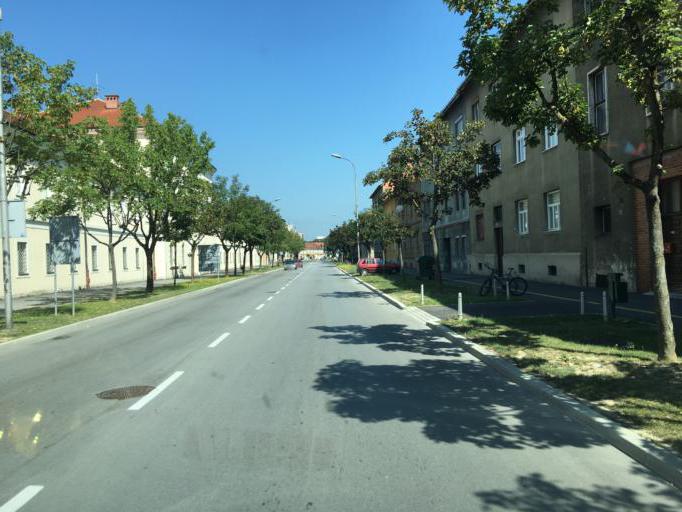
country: HR
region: Karlovacka
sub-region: Grad Karlovac
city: Karlovac
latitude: 45.4892
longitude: 15.5532
